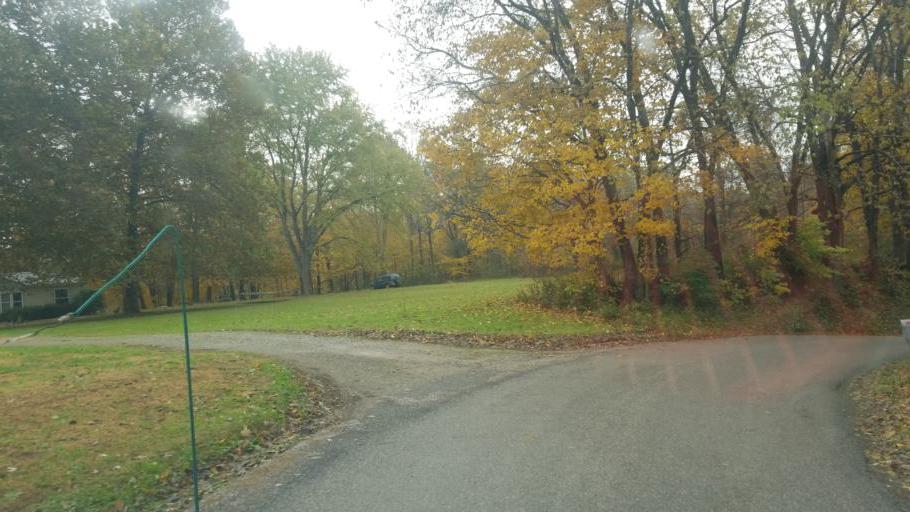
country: US
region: Ohio
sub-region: Washington County
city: Beverly
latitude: 39.5307
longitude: -81.7336
